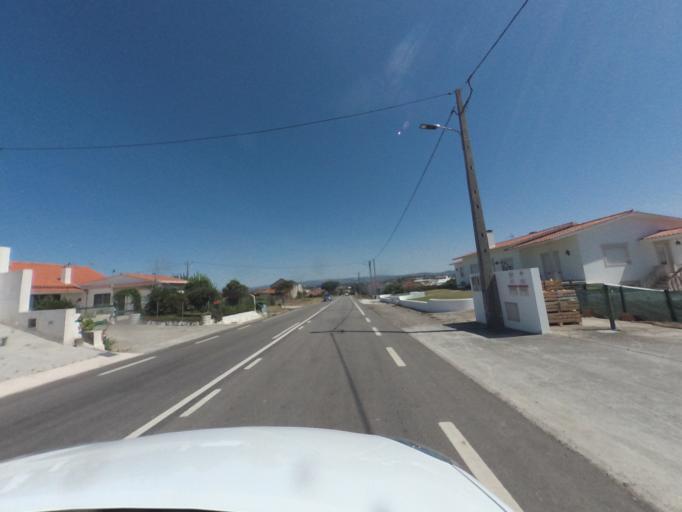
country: PT
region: Leiria
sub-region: Alcobaca
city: Alcobaca
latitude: 39.5200
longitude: -9.0247
